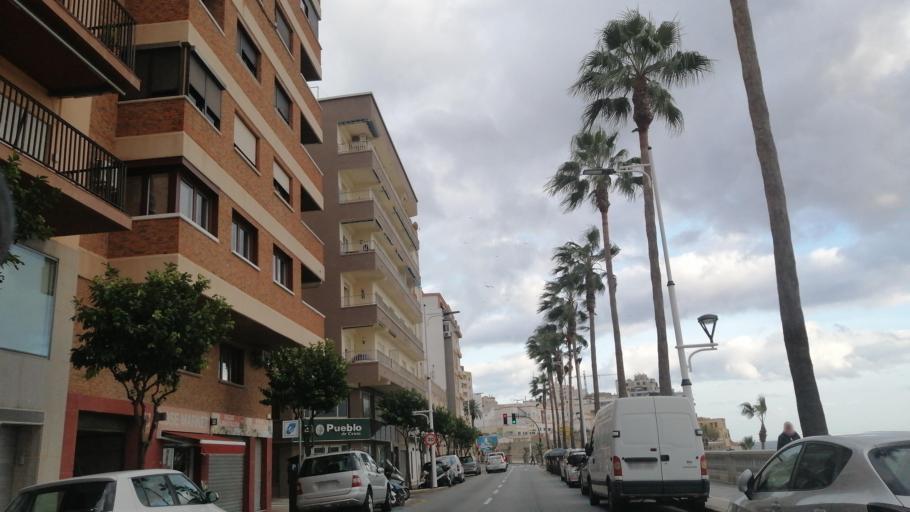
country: ES
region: Ceuta
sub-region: Ceuta
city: Ceuta
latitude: 35.8874
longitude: -5.3150
